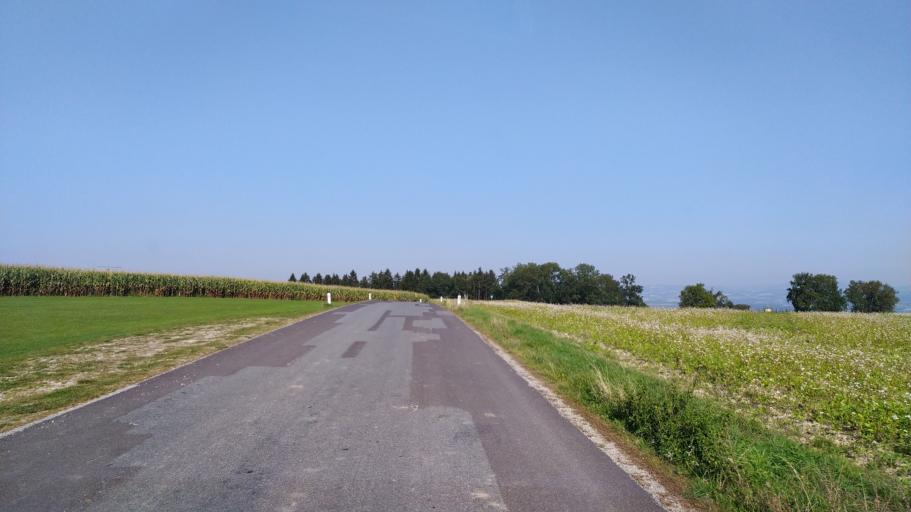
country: AT
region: Lower Austria
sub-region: Politischer Bezirk Amstetten
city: Zeillern
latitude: 48.1255
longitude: 14.7539
